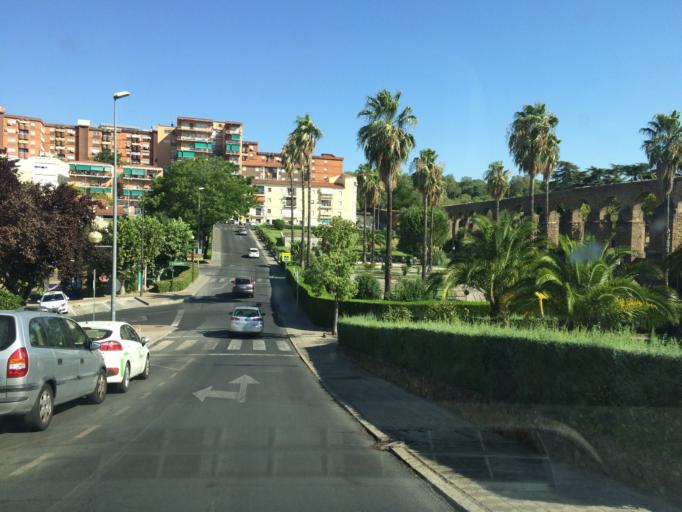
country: ES
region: Extremadura
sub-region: Provincia de Caceres
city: Plasencia
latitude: 40.0353
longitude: -6.0858
